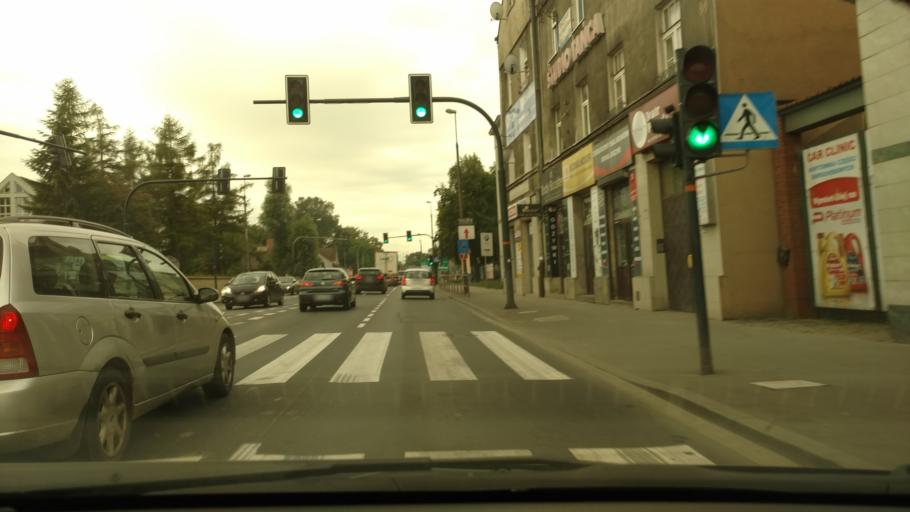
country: PL
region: Lesser Poland Voivodeship
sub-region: Krakow
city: Krakow
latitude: 50.0893
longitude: 19.9580
